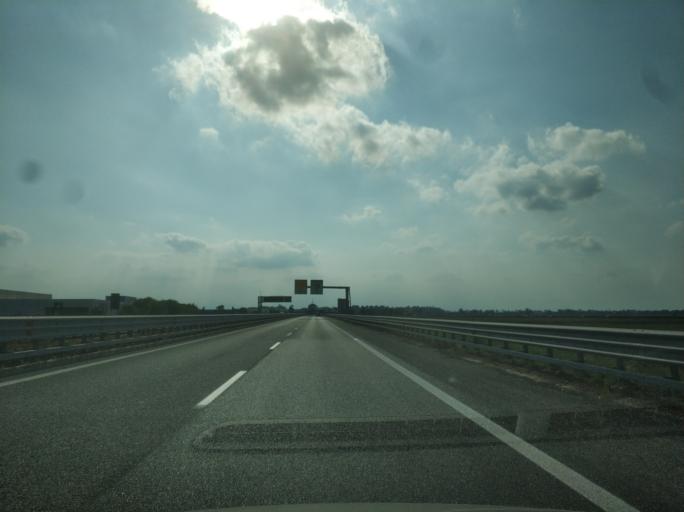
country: IT
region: Piedmont
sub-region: Provincia di Cuneo
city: Cervere
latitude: 44.6639
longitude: 7.7908
